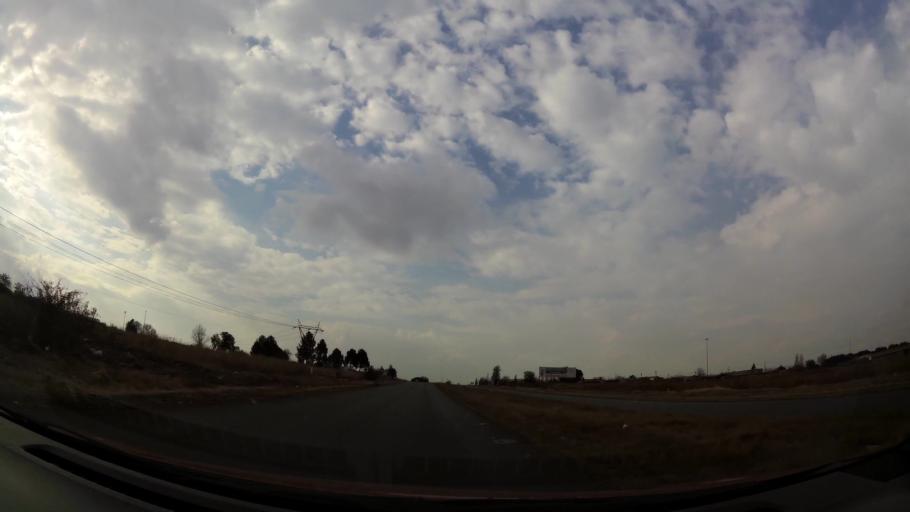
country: ZA
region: Gauteng
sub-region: Sedibeng District Municipality
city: Vanderbijlpark
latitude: -26.6629
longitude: 27.8430
